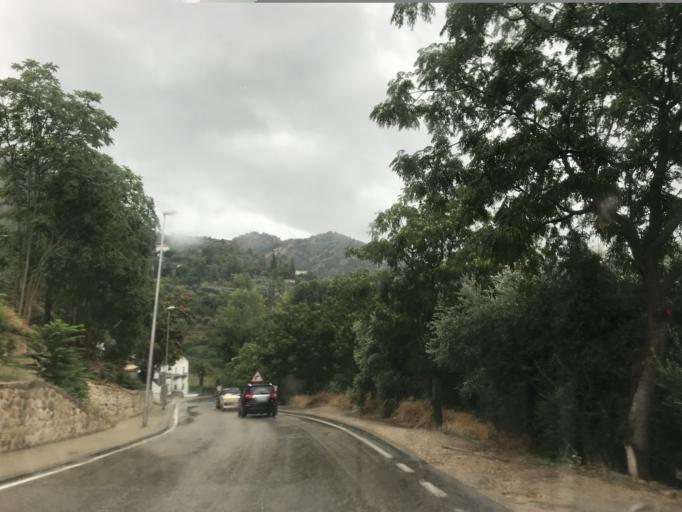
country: ES
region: Andalusia
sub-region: Provincia de Jaen
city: Cazorla
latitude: 37.9132
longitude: -3.0088
